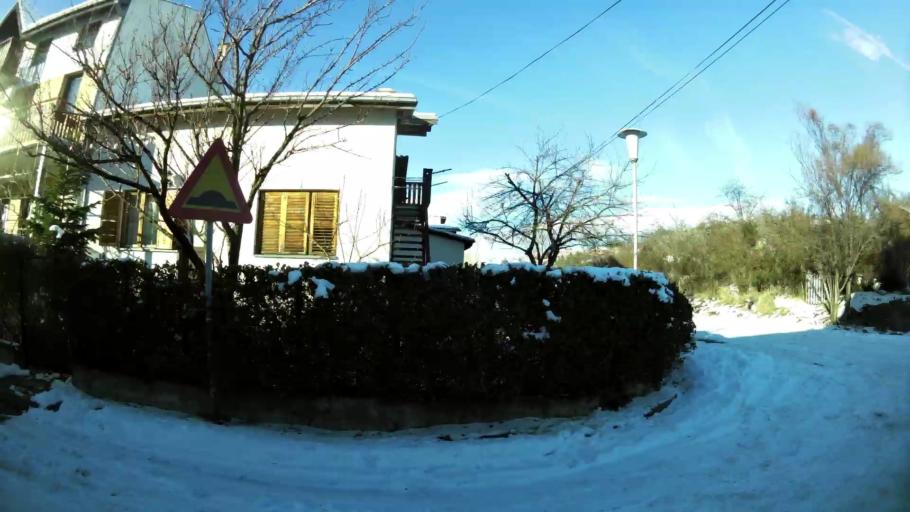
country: MK
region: Saraj
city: Saraj
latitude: 42.0092
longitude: 21.3319
